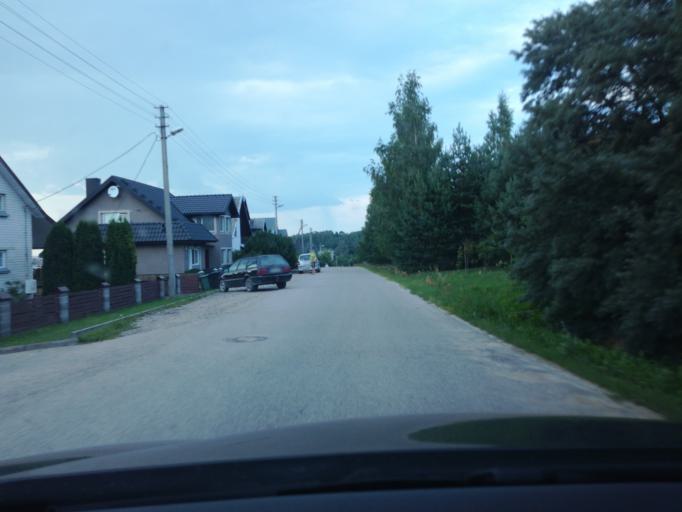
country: LT
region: Alytaus apskritis
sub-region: Alytus
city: Alytus
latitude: 54.3972
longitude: 24.0023
